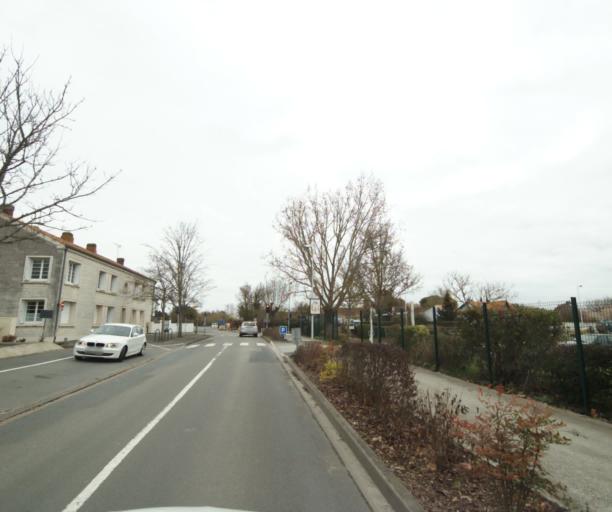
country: FR
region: Poitou-Charentes
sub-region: Departement de la Charente-Maritime
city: Lagord
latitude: 46.1911
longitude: -1.1570
